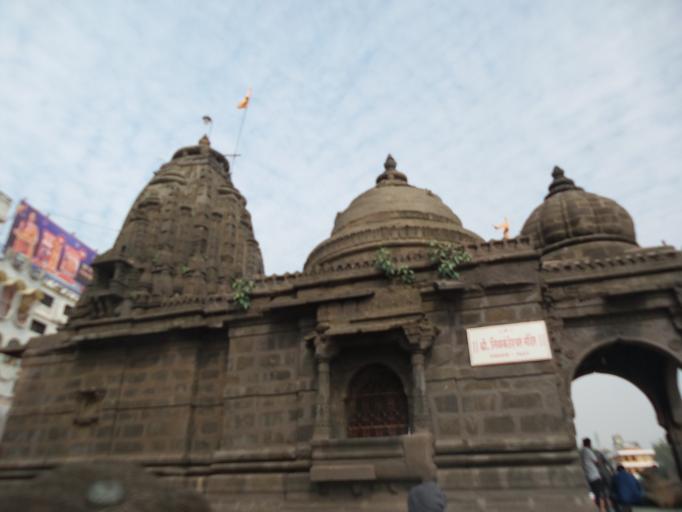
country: IN
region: Maharashtra
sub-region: Nashik Division
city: Nashik
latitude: 20.0064
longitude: 73.7922
